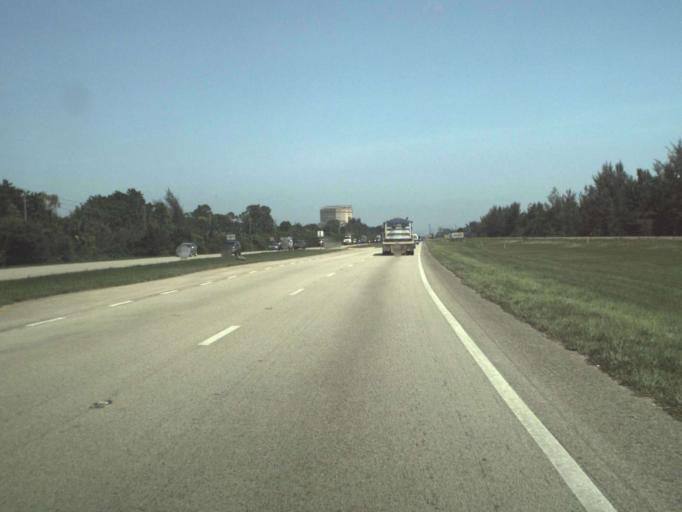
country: US
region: Florida
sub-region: Palm Beach County
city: Palm Beach Gardens
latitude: 26.7938
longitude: -80.1286
